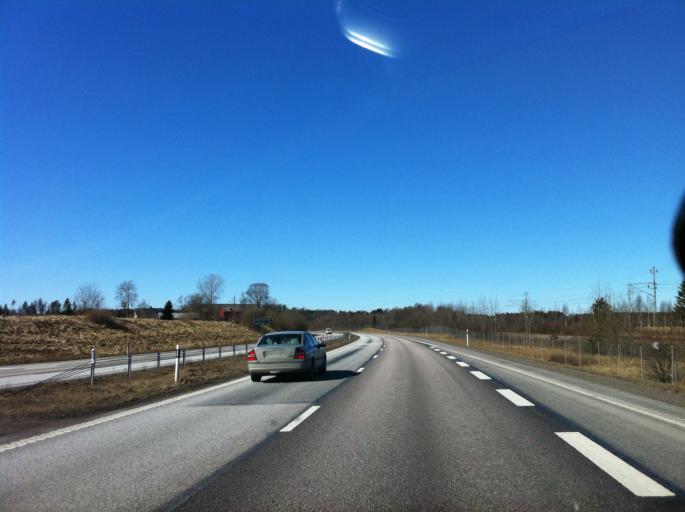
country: SE
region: Vaestra Goetaland
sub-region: Vanersborgs Kommun
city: Vanersborg
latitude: 58.3737
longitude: 12.3435
